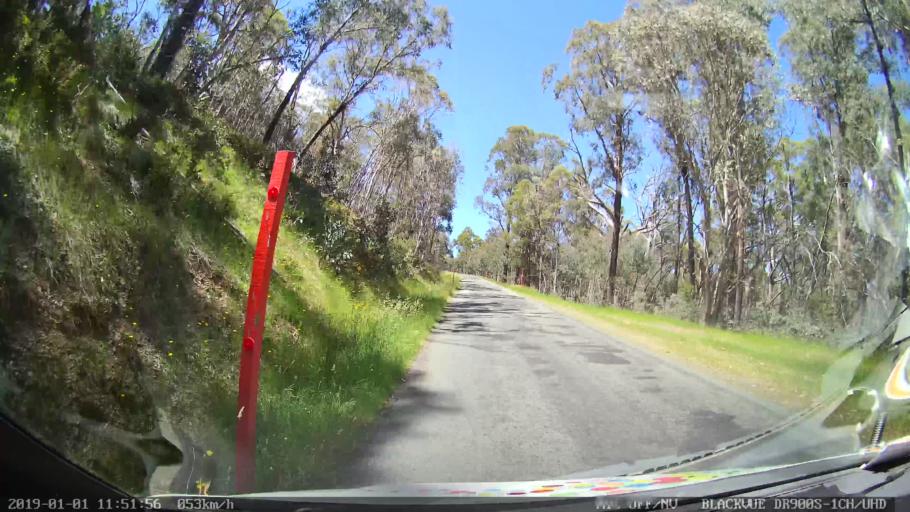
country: AU
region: New South Wales
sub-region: Snowy River
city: Jindabyne
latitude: -35.8861
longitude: 148.4326
